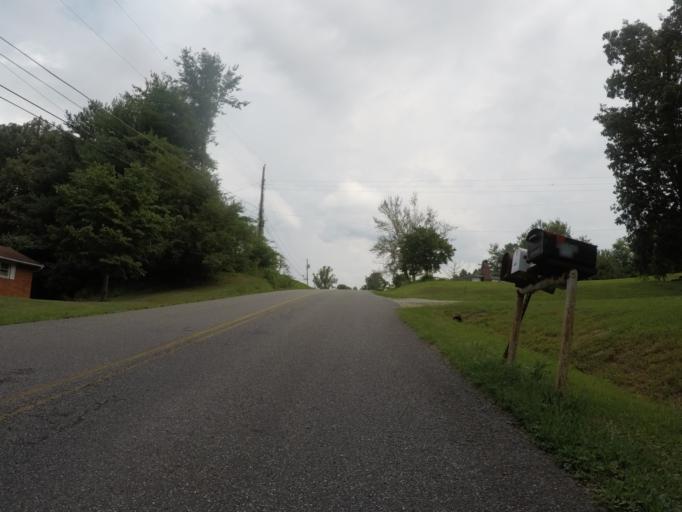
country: US
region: Kentucky
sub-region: Boyd County
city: Meads
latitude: 38.4203
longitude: -82.7076
